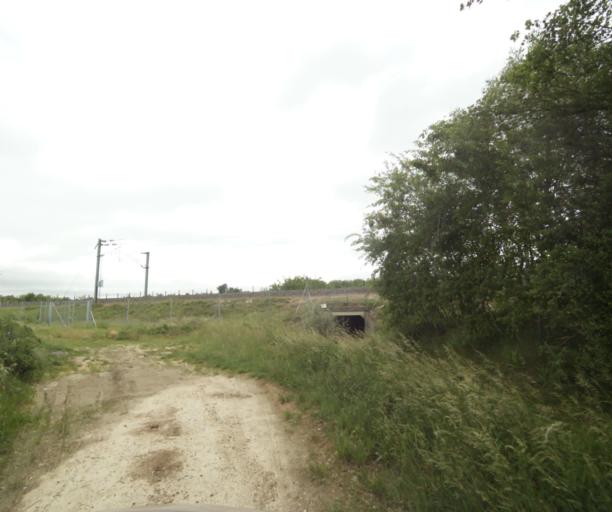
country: FR
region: Rhone-Alpes
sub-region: Departement de l'Ain
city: Tramoyes
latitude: 45.8581
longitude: 4.9529
